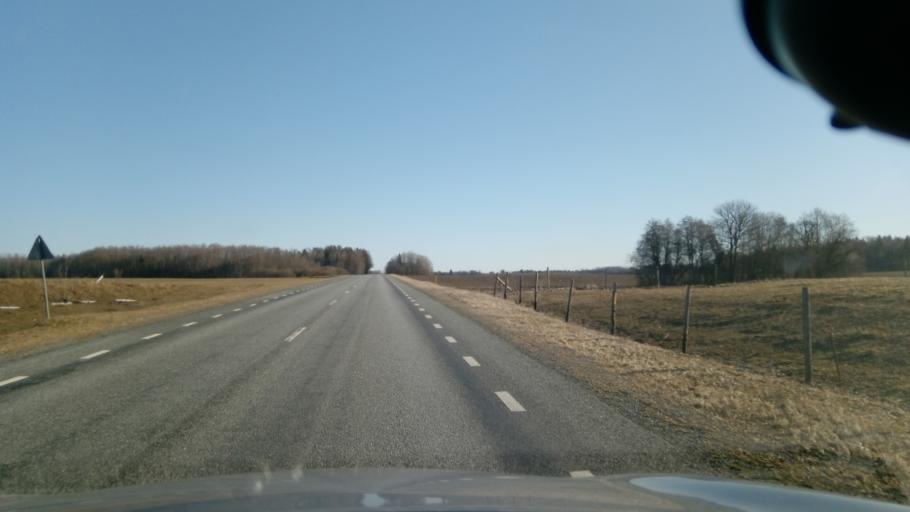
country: EE
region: Jaervamaa
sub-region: Jaerva-Jaani vald
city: Jarva-Jaani
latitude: 59.0835
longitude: 25.9671
